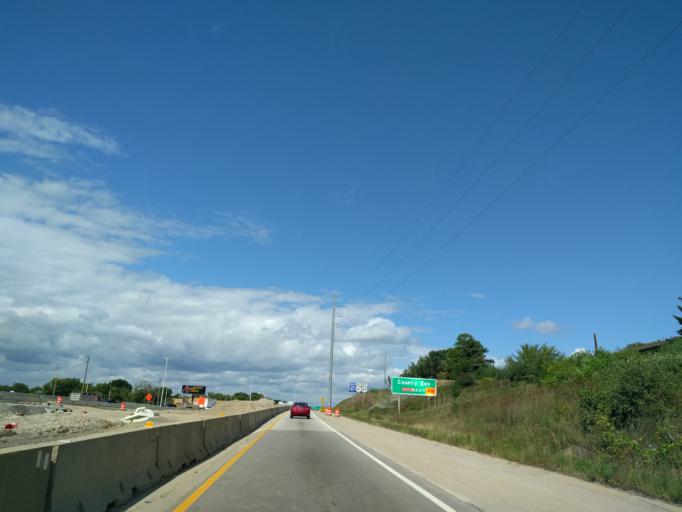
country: US
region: Wisconsin
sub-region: Milwaukee County
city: West Allis
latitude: 43.0307
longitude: -88.0327
